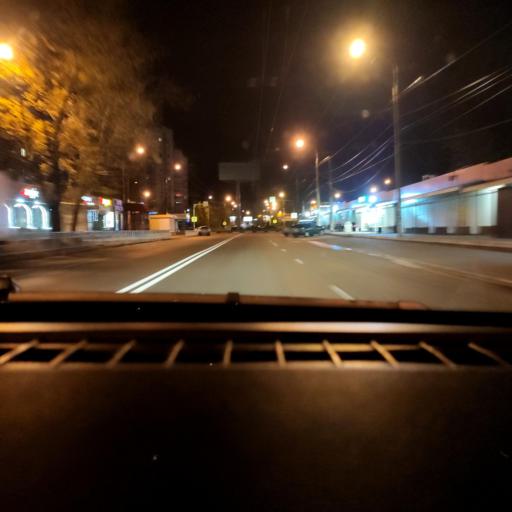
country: RU
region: Voronezj
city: Podgornoye
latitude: 51.7040
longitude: 39.1482
